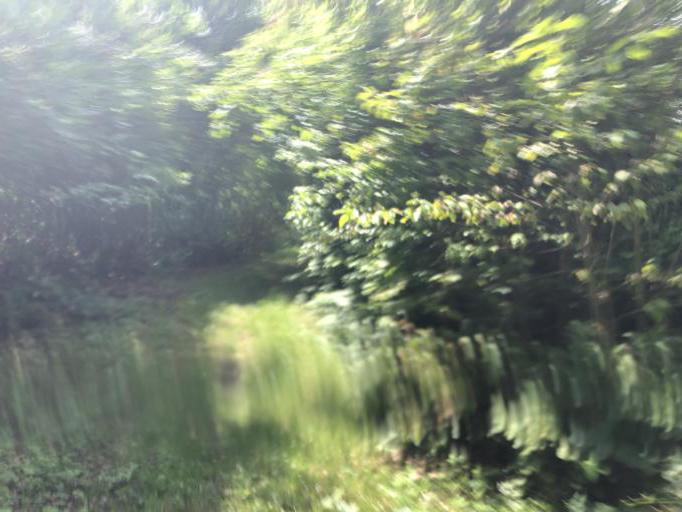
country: DE
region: Bavaria
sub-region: Regierungsbezirk Mittelfranken
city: Erlangen
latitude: 49.5808
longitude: 10.9601
